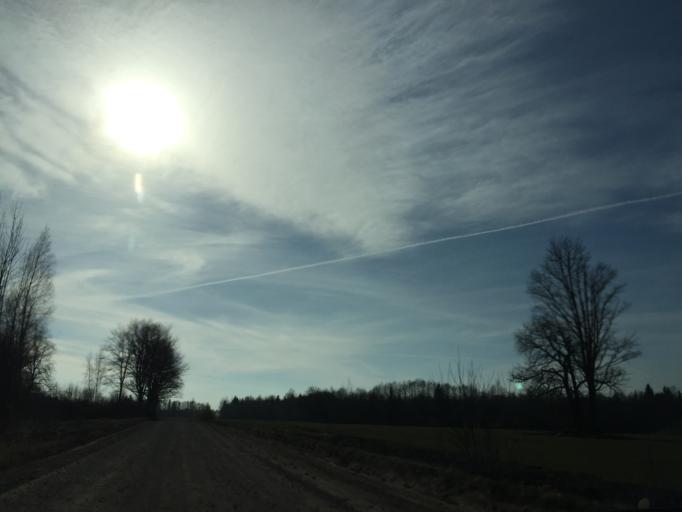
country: LV
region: Saulkrastu
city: Saulkrasti
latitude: 57.2997
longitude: 24.5506
